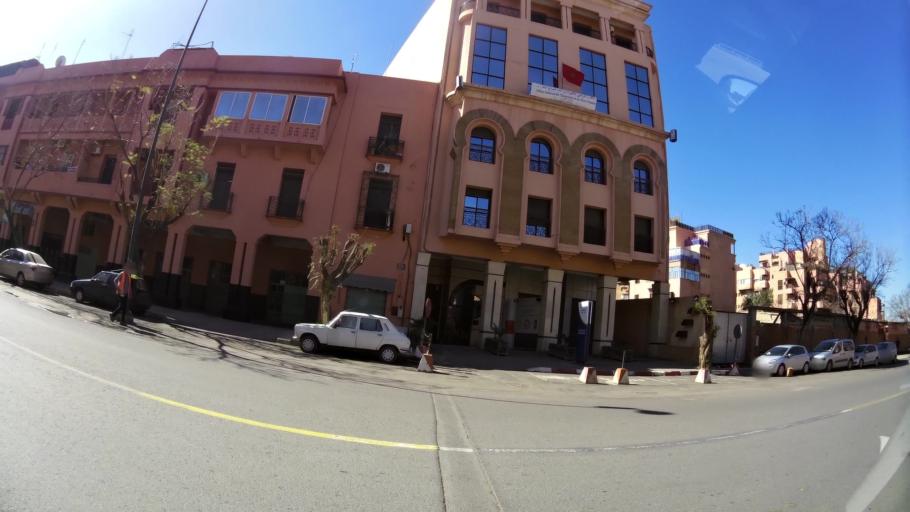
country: MA
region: Marrakech-Tensift-Al Haouz
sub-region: Marrakech
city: Marrakesh
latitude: 31.6326
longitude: -8.0151
